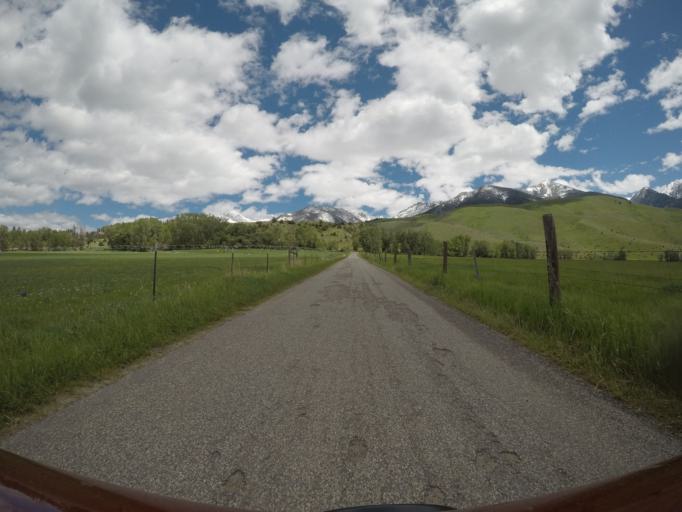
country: US
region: Montana
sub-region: Park County
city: Livingston
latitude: 45.4967
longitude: -110.5634
